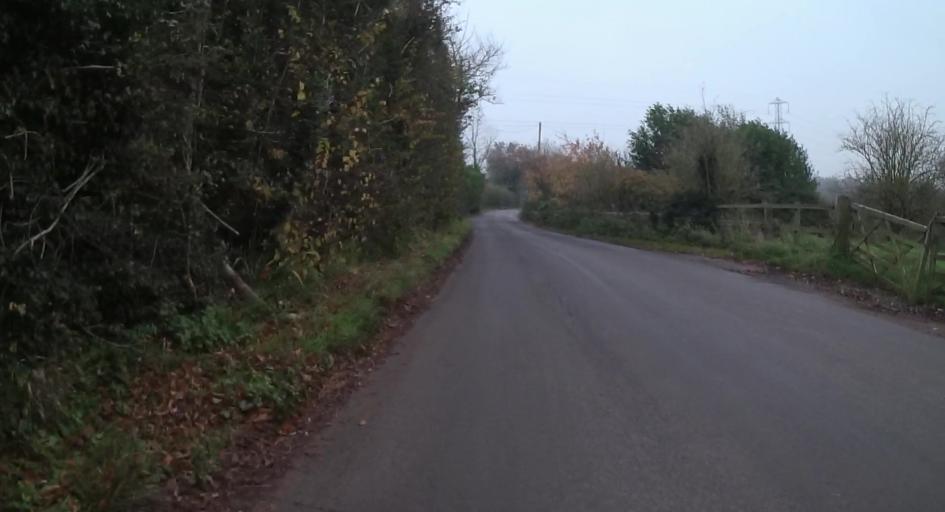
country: GB
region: England
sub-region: Hampshire
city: Long Sutton
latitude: 51.1892
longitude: -0.9047
